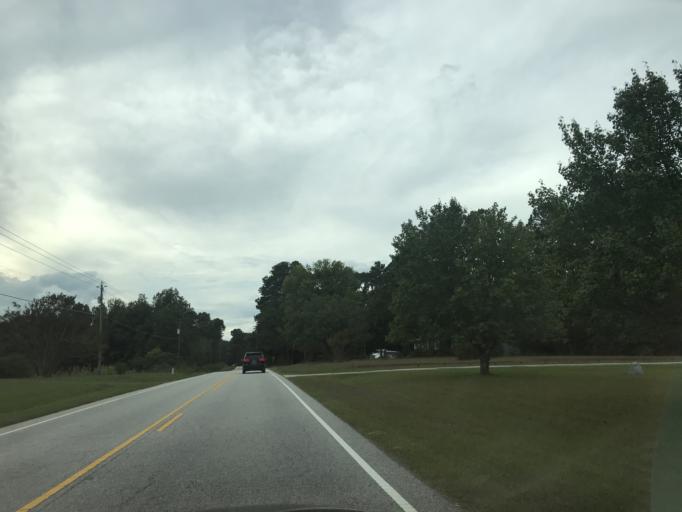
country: US
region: North Carolina
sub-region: Franklin County
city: Youngsville
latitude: 35.9983
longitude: -78.4211
